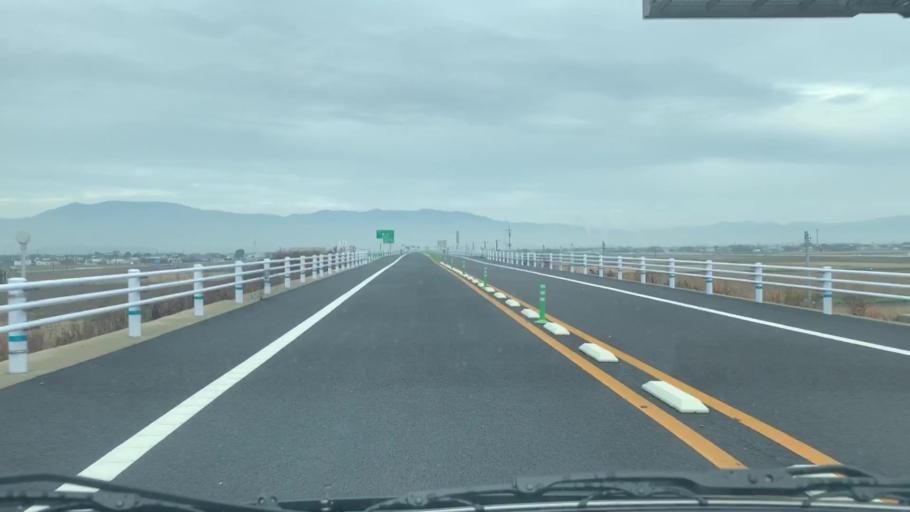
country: JP
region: Saga Prefecture
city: Saga-shi
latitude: 33.2082
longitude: 130.2151
